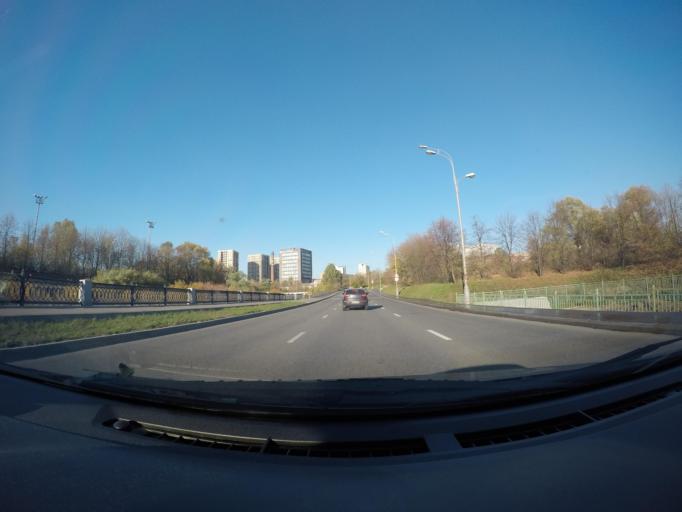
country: RU
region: Moskovskaya
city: Bogorodskoye
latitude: 55.8045
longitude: 37.7015
